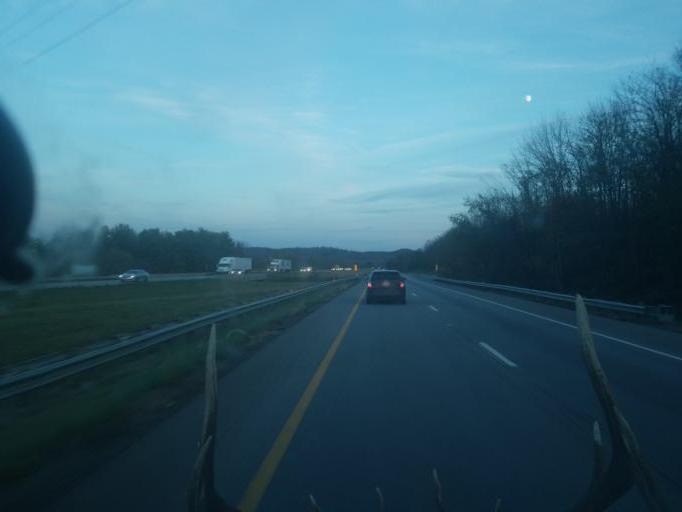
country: US
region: Ohio
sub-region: Muskingum County
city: New Concord
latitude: 39.9854
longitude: -81.7037
